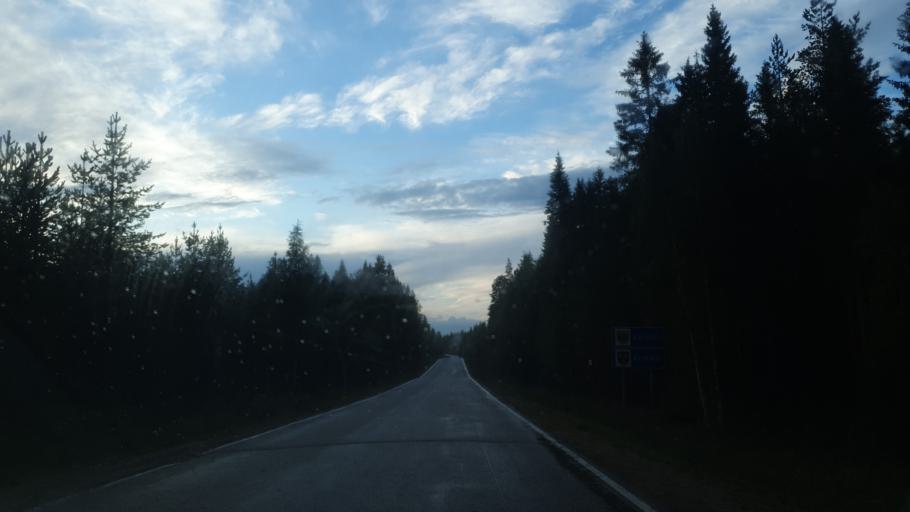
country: FI
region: North Karelia
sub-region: Pielisen Karjala
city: Lieksa
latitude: 63.7406
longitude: 29.8566
